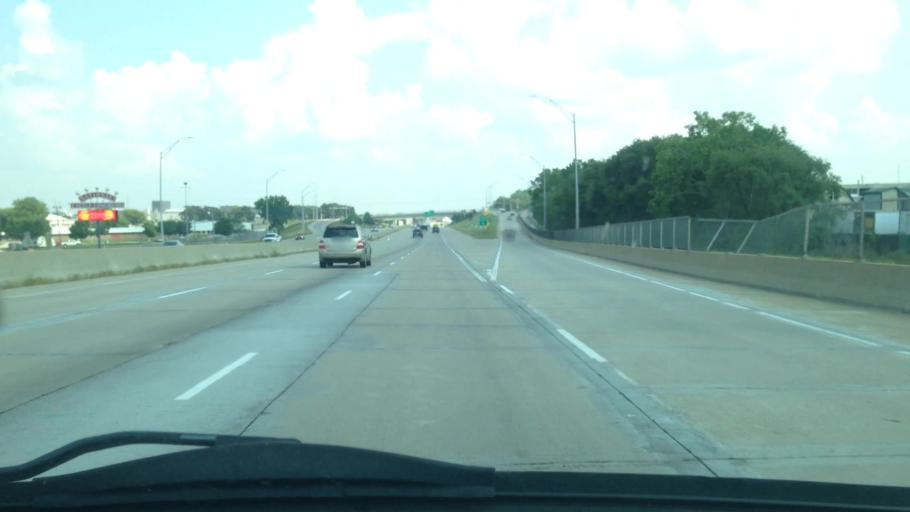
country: US
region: Iowa
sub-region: Black Hawk County
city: Waterloo
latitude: 42.5114
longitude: -92.3812
